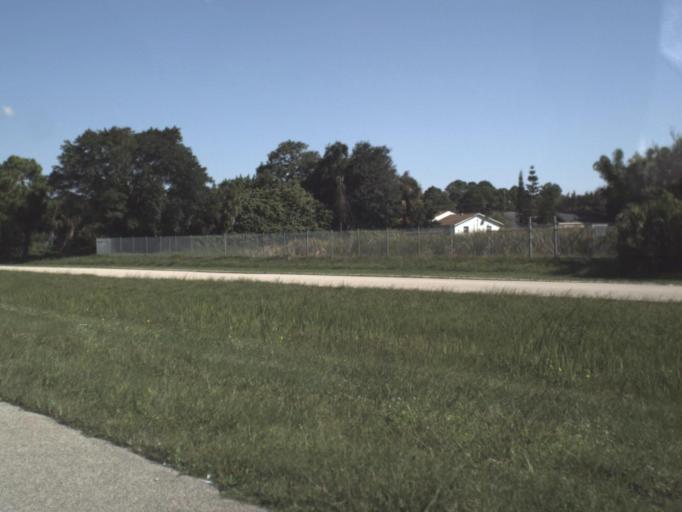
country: US
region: Florida
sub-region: Charlotte County
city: Rotonda
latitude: 26.9326
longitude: -82.2598
